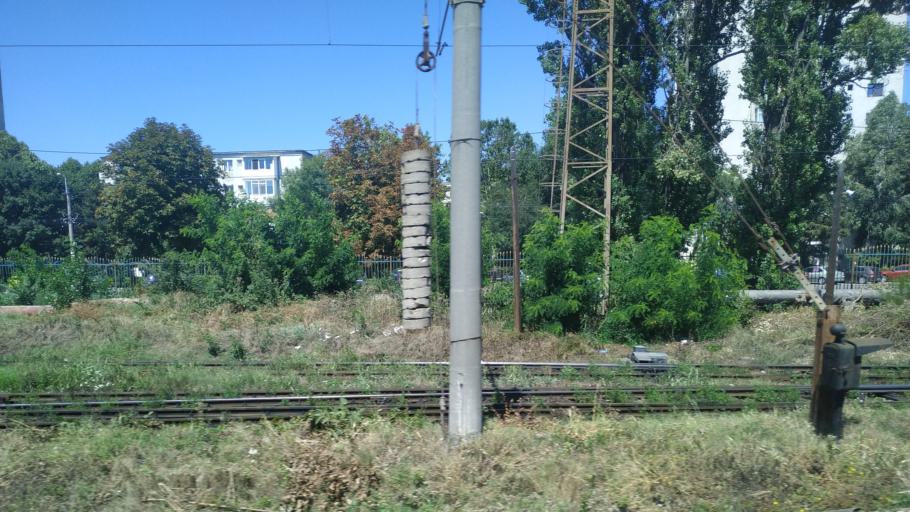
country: RO
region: Constanta
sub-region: Municipiul Constanta
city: Constanta
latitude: 44.1710
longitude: 28.6200
